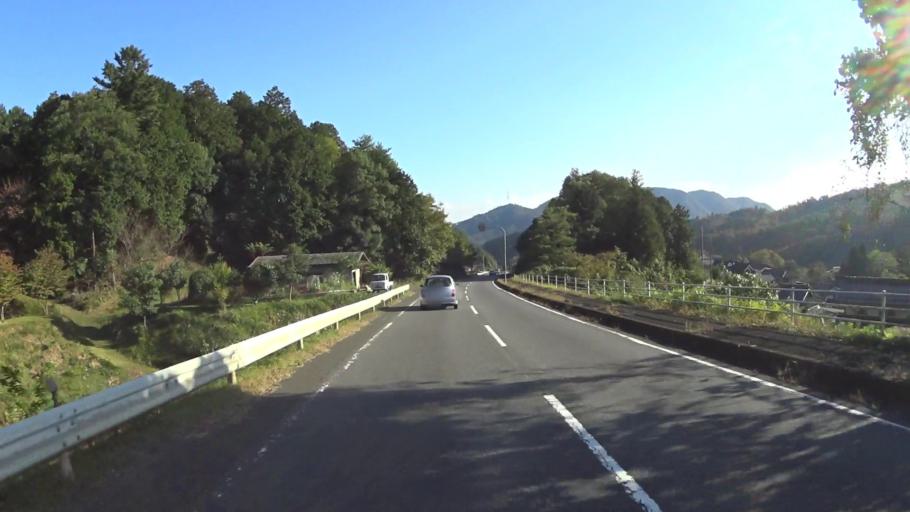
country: JP
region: Kyoto
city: Fukuchiyama
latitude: 35.3793
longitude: 135.0979
